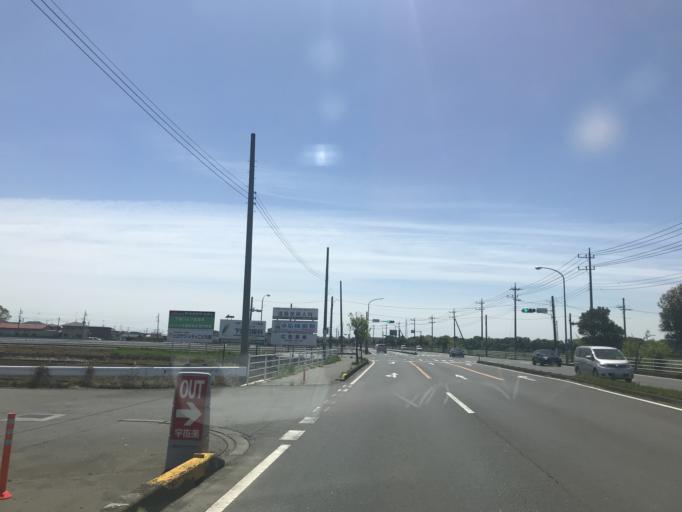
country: JP
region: Ibaraki
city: Shimodate
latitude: 36.2902
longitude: 139.9708
